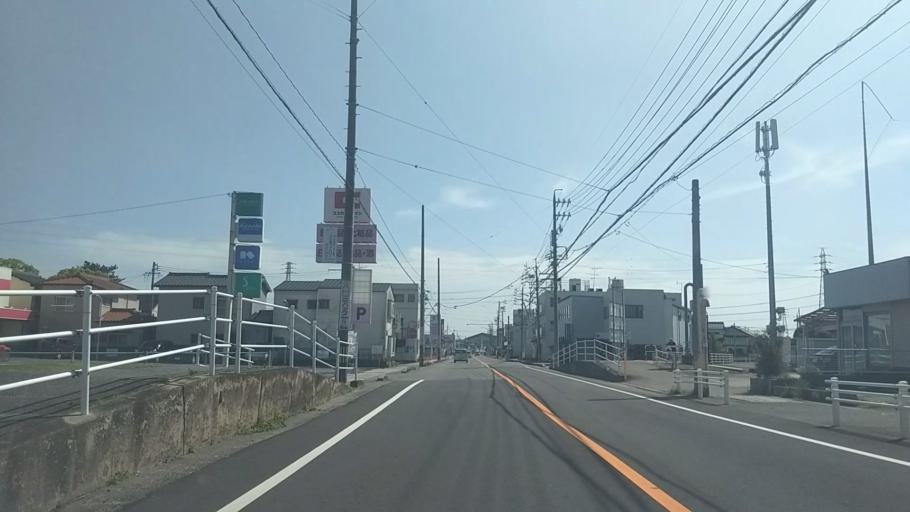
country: JP
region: Aichi
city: Okazaki
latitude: 34.9720
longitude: 137.1331
